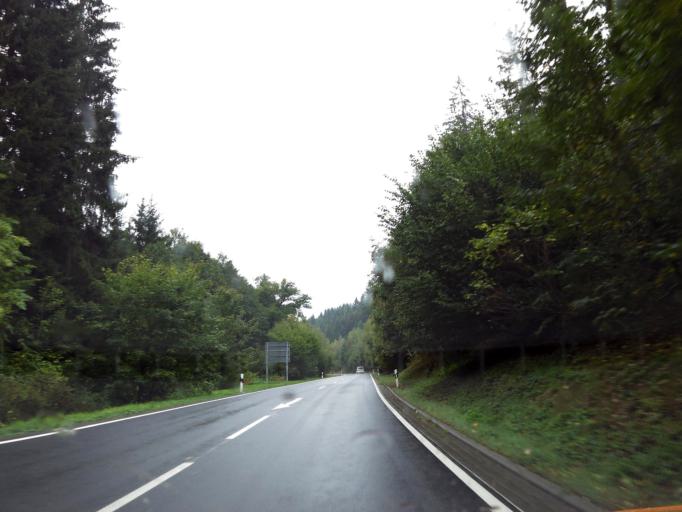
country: DE
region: Saxony-Anhalt
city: Harzgerode
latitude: 51.6453
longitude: 11.1053
